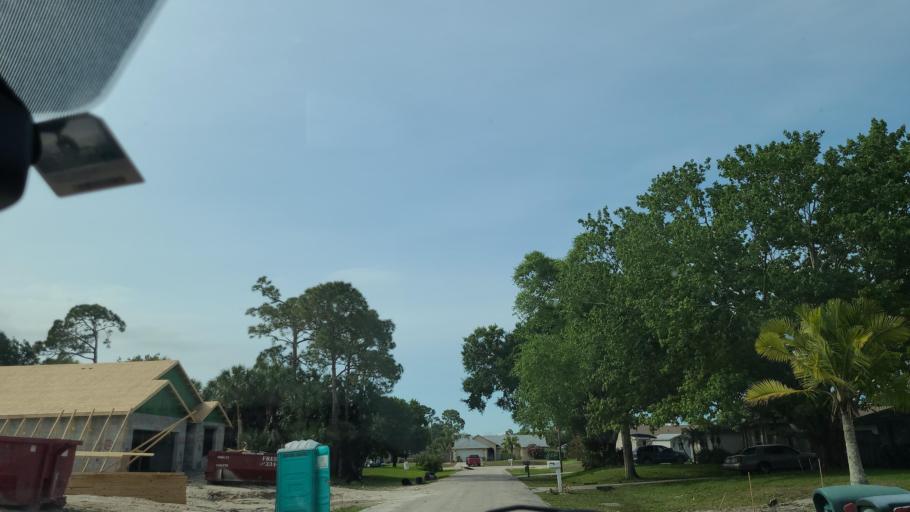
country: US
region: Florida
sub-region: Indian River County
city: Sebastian
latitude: 27.7612
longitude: -80.4759
